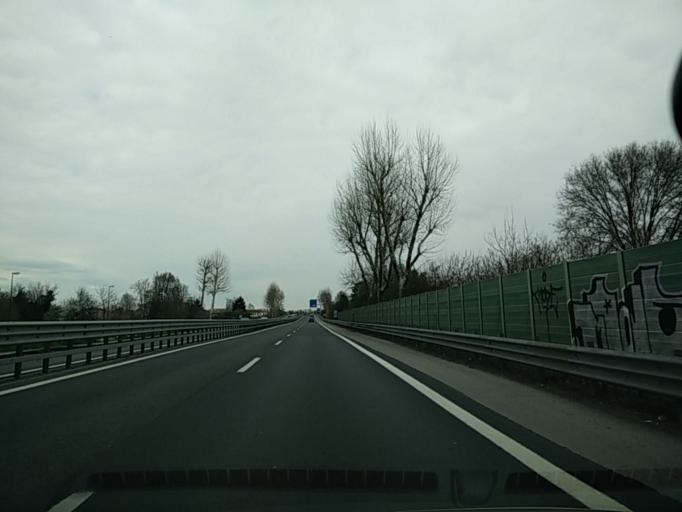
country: IT
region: Veneto
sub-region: Provincia di Treviso
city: Dosson
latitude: 45.6510
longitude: 12.2515
